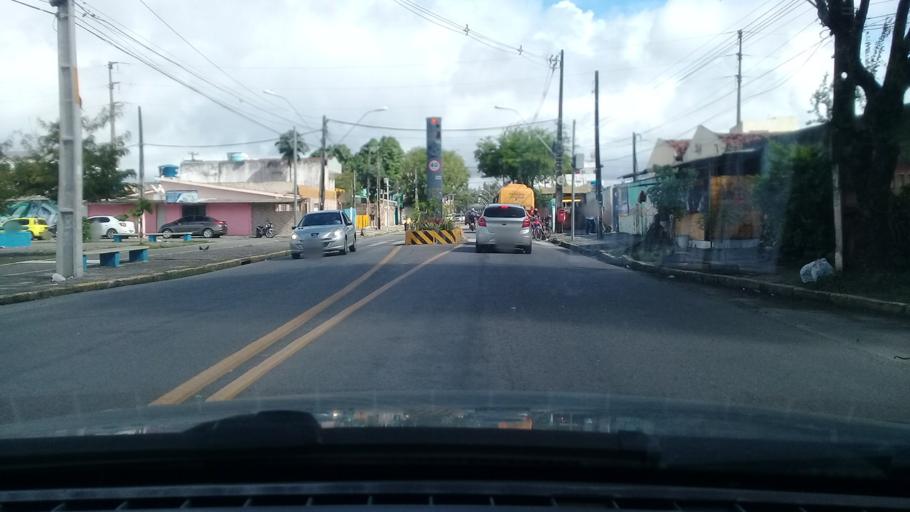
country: BR
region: Pernambuco
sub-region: Recife
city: Recife
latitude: -8.0670
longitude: -34.9278
